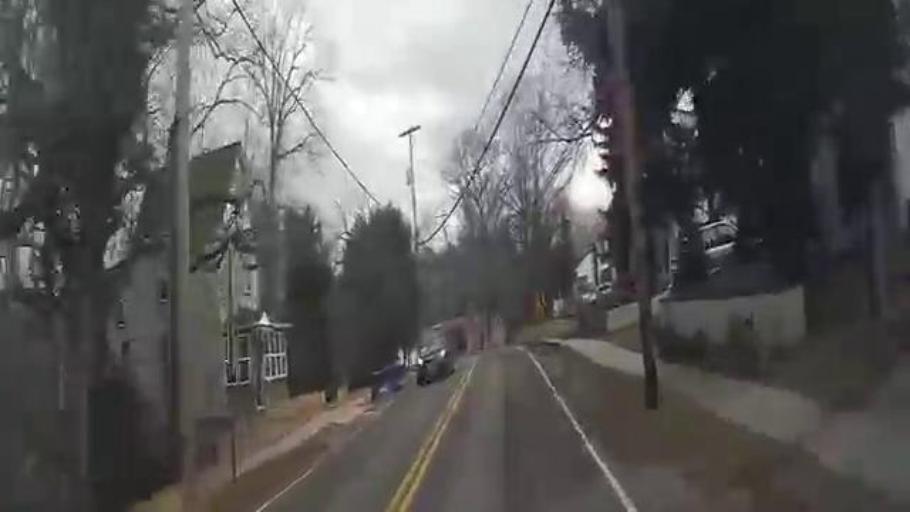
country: US
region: New Jersey
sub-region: Camden County
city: Clementon
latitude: 39.8026
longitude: -74.9800
